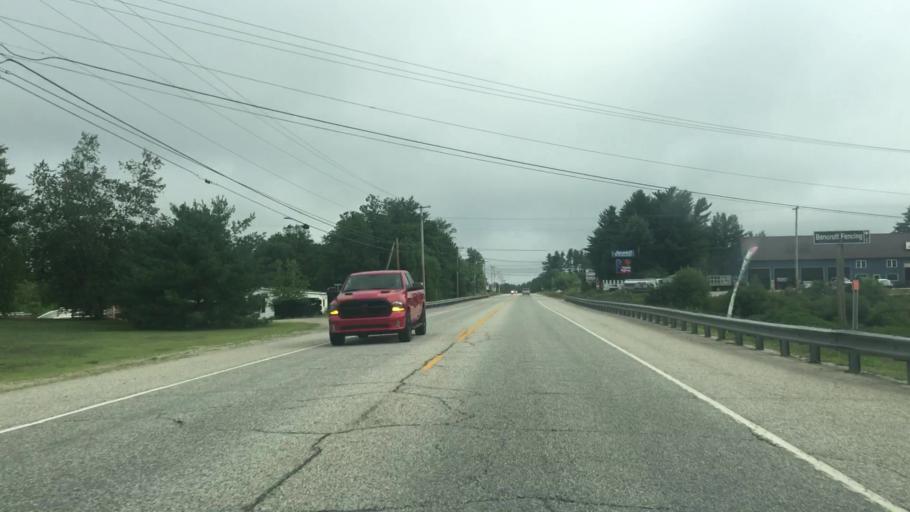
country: US
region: Maine
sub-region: Oxford County
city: South Paris
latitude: 44.2385
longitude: -70.5138
